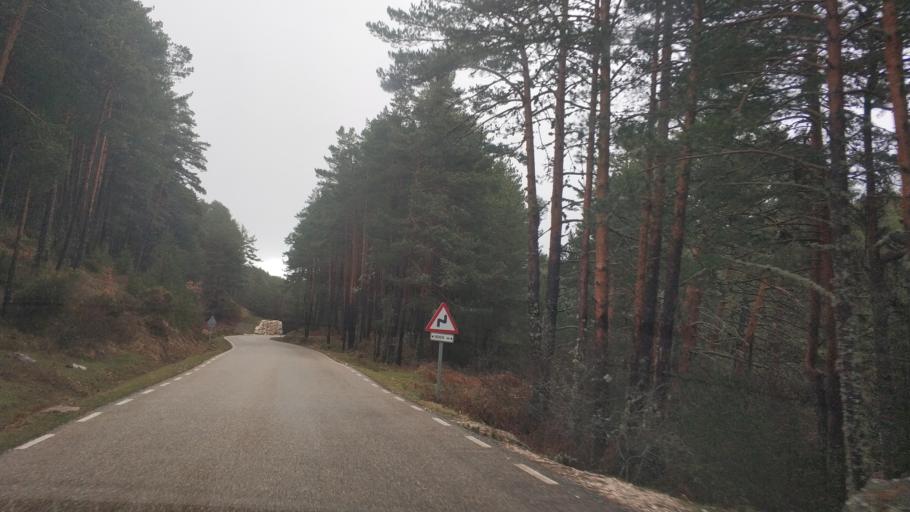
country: ES
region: Castille and Leon
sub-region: Provincia de Burgos
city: Neila
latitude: 42.0219
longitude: -3.0144
